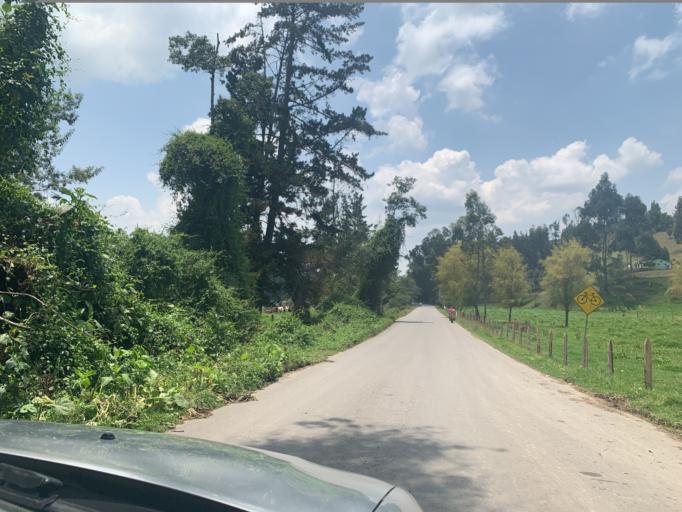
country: CO
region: Boyaca
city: Chiquinquira
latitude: 5.5386
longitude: -73.7473
